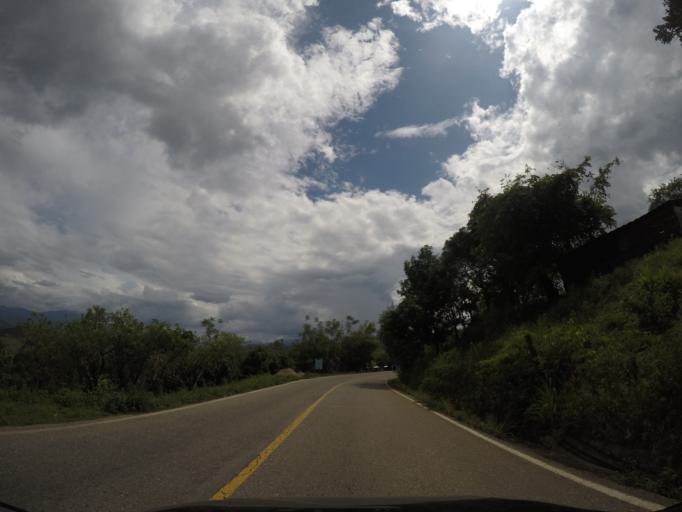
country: MX
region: Oaxaca
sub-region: San Jeronimo Coatlan
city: San Cristobal Honduras
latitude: 16.4325
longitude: -97.0639
